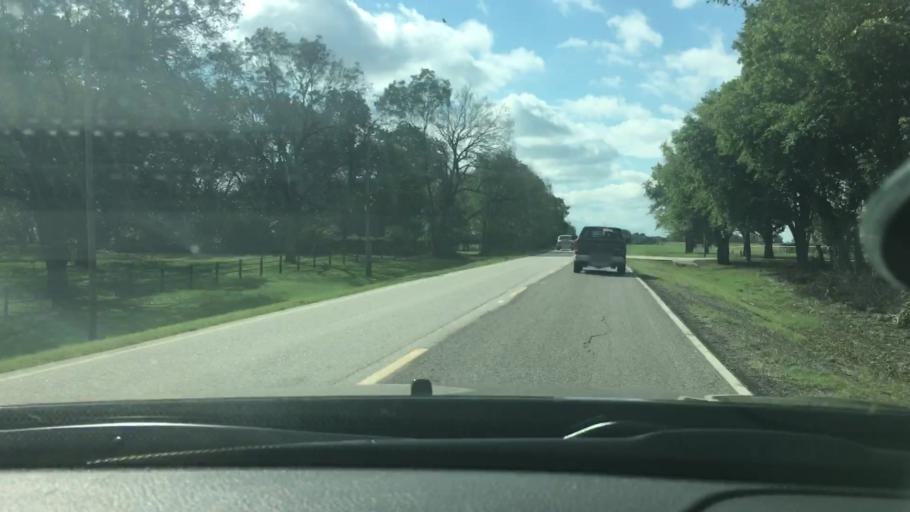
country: US
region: Oklahoma
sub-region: Pontotoc County
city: Ada
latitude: 34.7008
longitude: -96.6349
